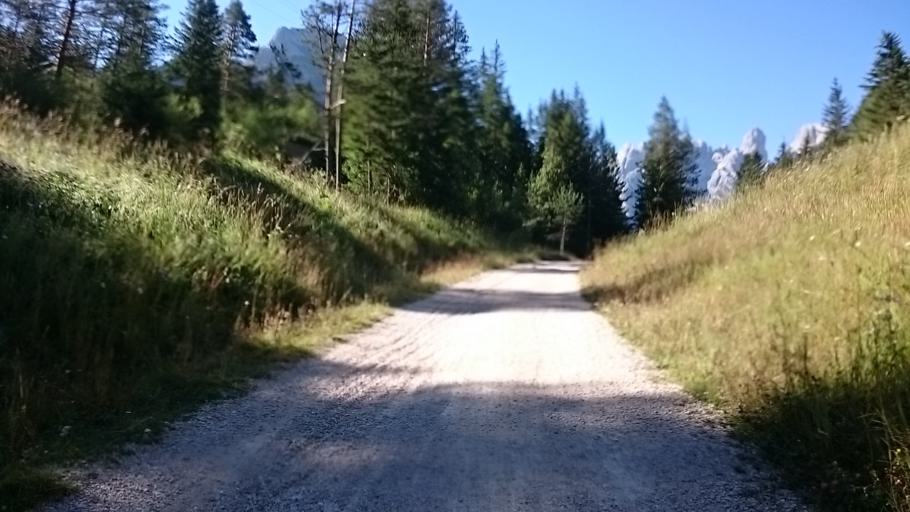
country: IT
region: Trentino-Alto Adige
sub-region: Bolzano
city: Dobbiaco
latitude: 46.6454
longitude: 12.2327
